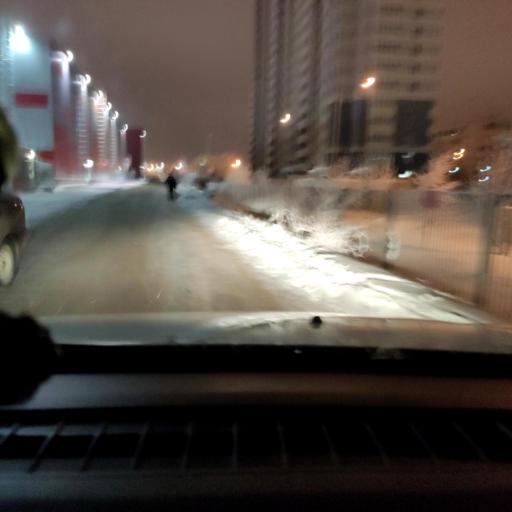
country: RU
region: Samara
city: Samara
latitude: 53.2528
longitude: 50.2157
